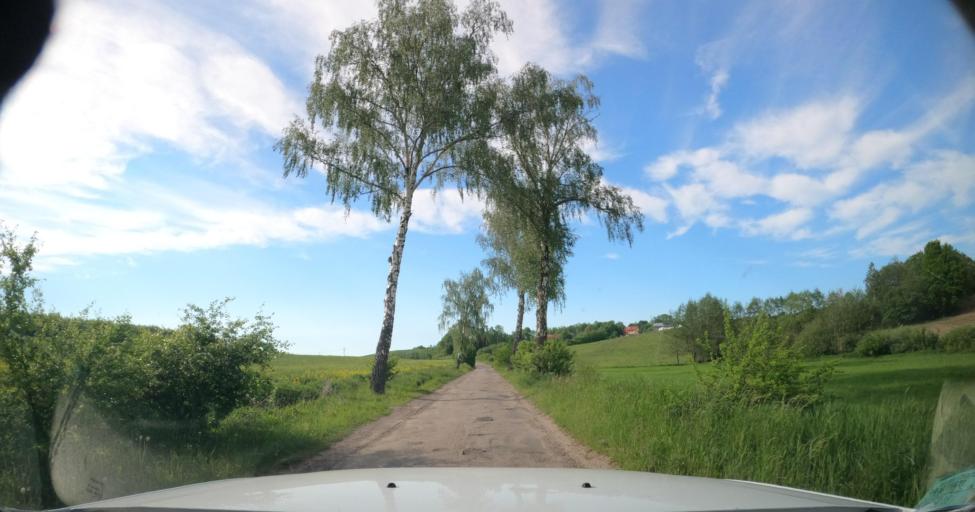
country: PL
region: Warmian-Masurian Voivodeship
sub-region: Powiat ostrodzki
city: Morag
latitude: 54.0573
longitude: 19.8885
